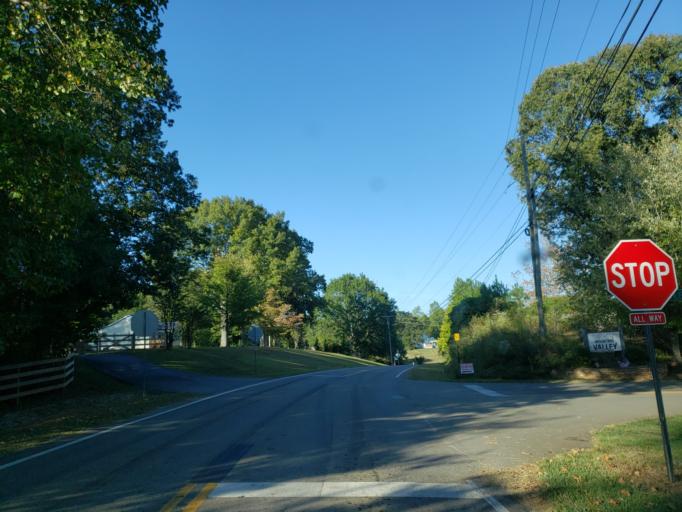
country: US
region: Georgia
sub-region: Pickens County
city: Nelson
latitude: 34.3994
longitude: -84.3994
